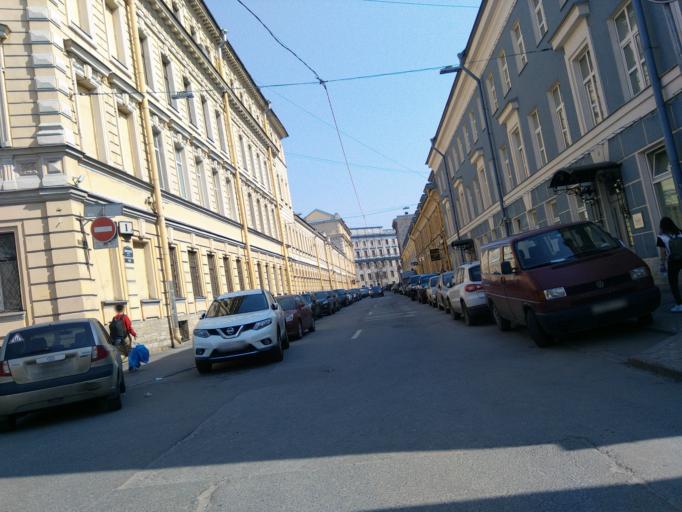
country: RU
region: St.-Petersburg
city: Saint Petersburg
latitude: 59.9454
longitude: 30.2916
